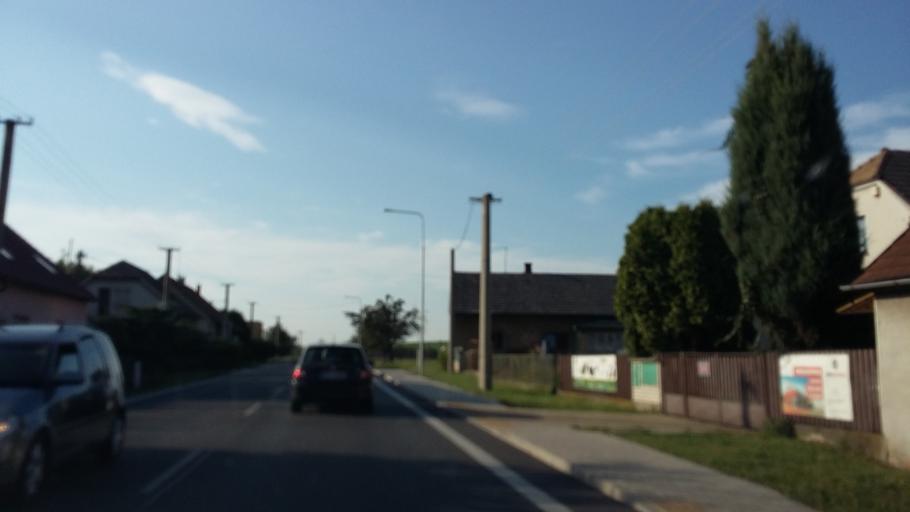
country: CZ
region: Central Bohemia
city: Lustenice
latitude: 50.2741
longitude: 14.9598
